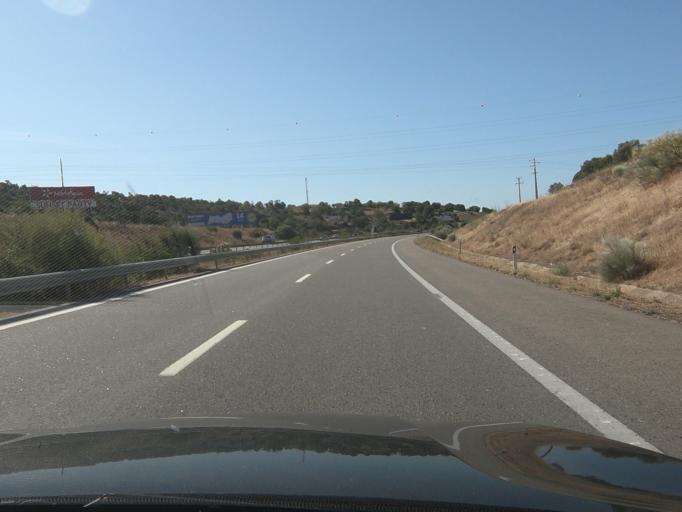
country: PT
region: Faro
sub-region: Albufeira
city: Ferreiras
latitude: 37.1862
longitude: -8.2185
